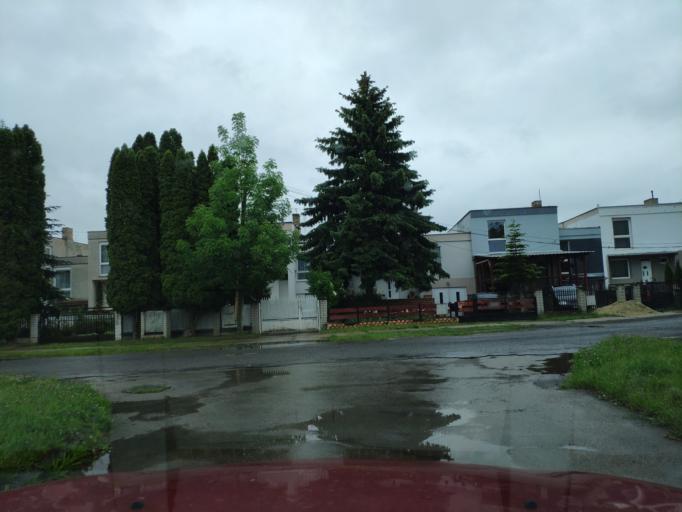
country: SK
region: Kosicky
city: Cierna nad Tisou
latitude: 48.4149
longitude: 22.0866
